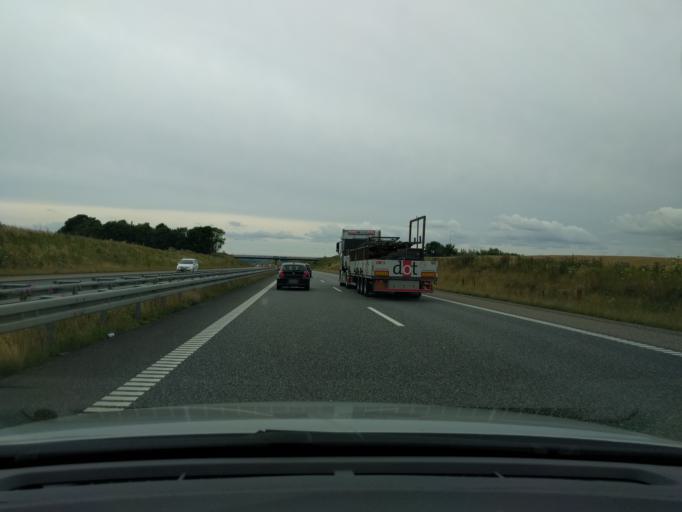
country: DK
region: Central Jutland
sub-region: Hedensted Kommune
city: Torring
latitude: 55.8245
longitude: 9.5361
